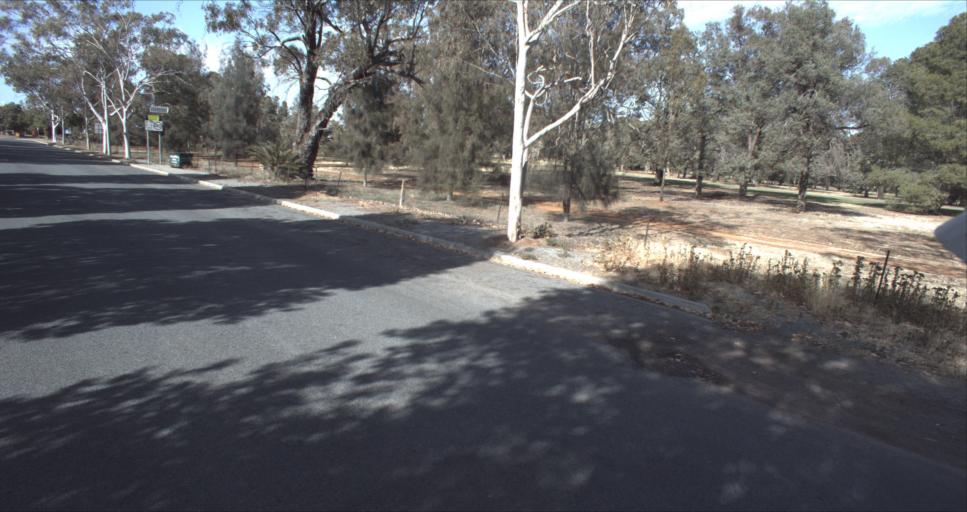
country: AU
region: New South Wales
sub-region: Leeton
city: Leeton
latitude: -34.5642
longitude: 146.4100
